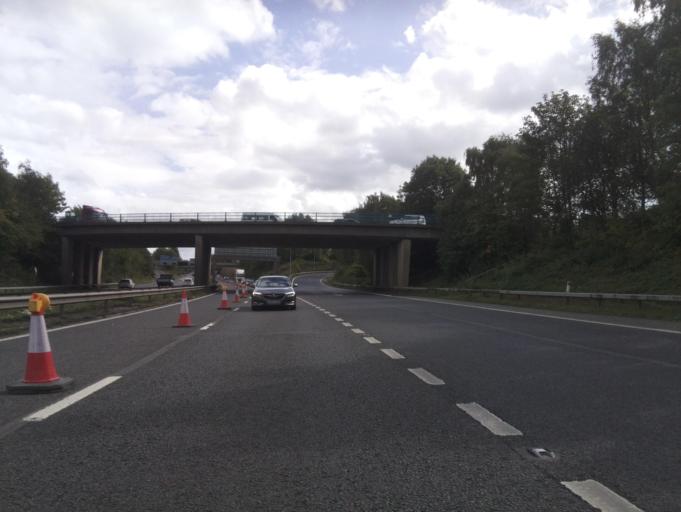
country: GB
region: England
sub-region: Borough of Tameside
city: Hyde
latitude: 53.4537
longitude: -2.0847
